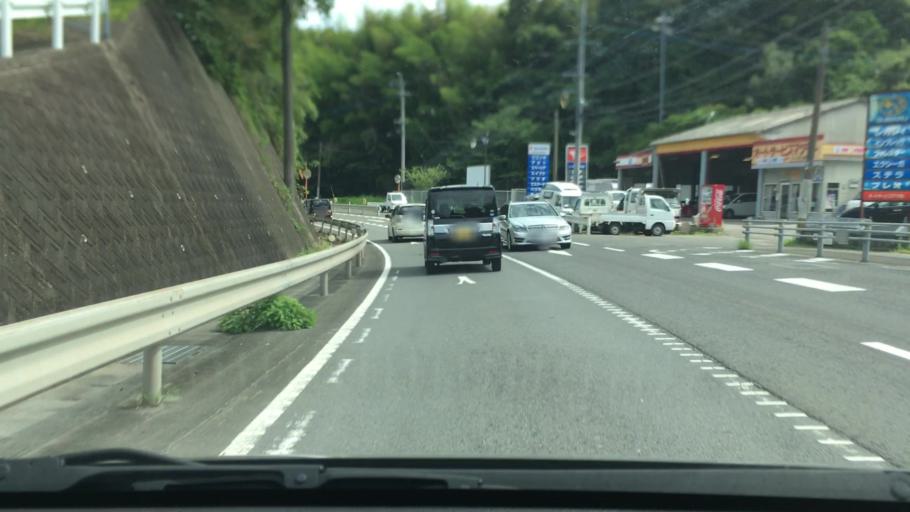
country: JP
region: Nagasaki
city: Togitsu
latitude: 32.9394
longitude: 129.7819
